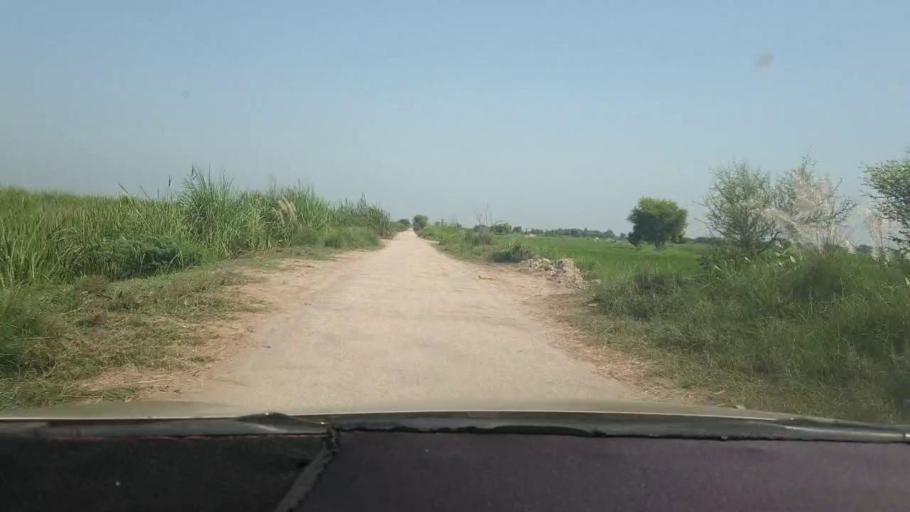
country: PK
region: Sindh
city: Miro Khan
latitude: 27.6974
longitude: 68.0946
